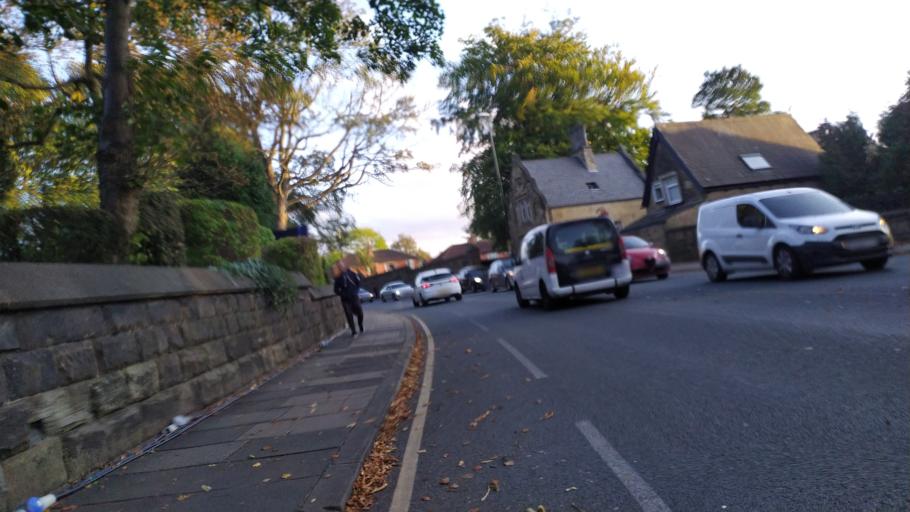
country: GB
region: England
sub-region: City and Borough of Leeds
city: Leeds
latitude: 53.8185
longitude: -1.5742
